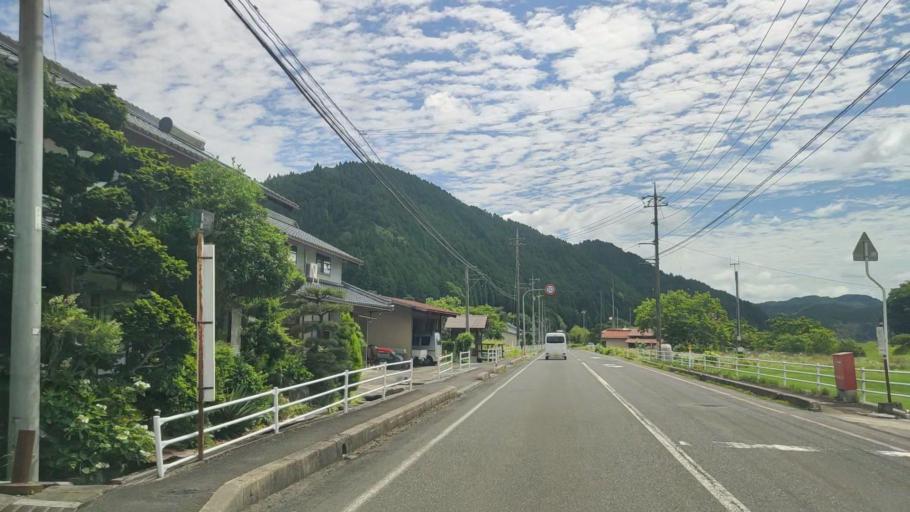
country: JP
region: Okayama
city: Niimi
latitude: 35.1627
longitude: 133.5862
